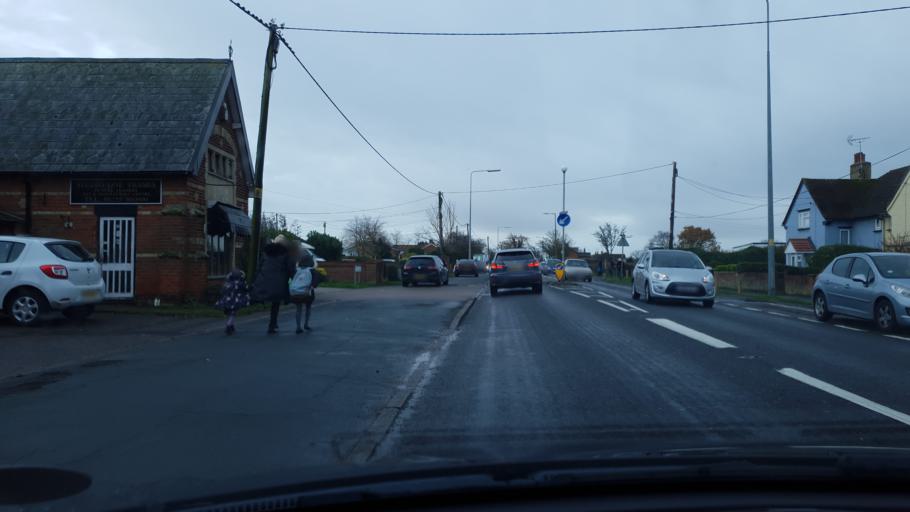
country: GB
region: England
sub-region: Essex
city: Little Clacton
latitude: 51.8247
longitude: 1.1420
